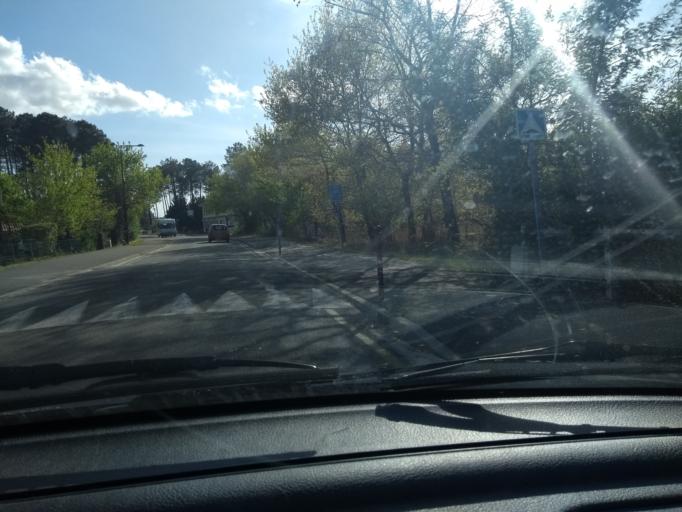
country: FR
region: Aquitaine
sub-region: Departement des Landes
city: Parentis-en-Born
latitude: 44.3445
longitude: -1.0965
